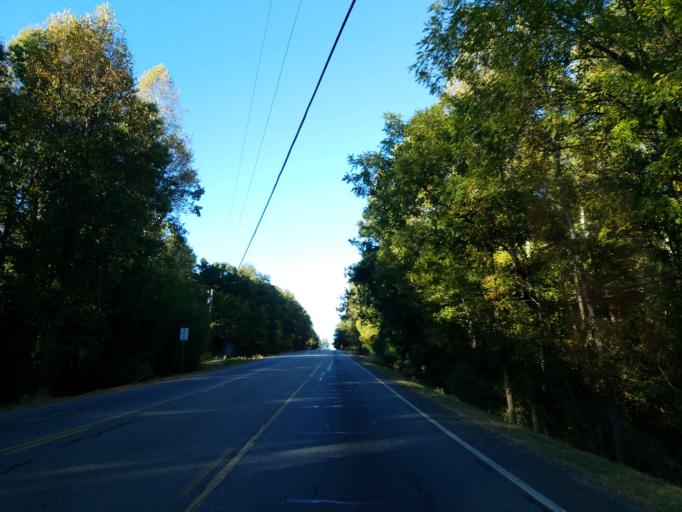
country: US
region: Georgia
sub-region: Cherokee County
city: Ball Ground
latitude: 34.3568
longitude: -84.3785
